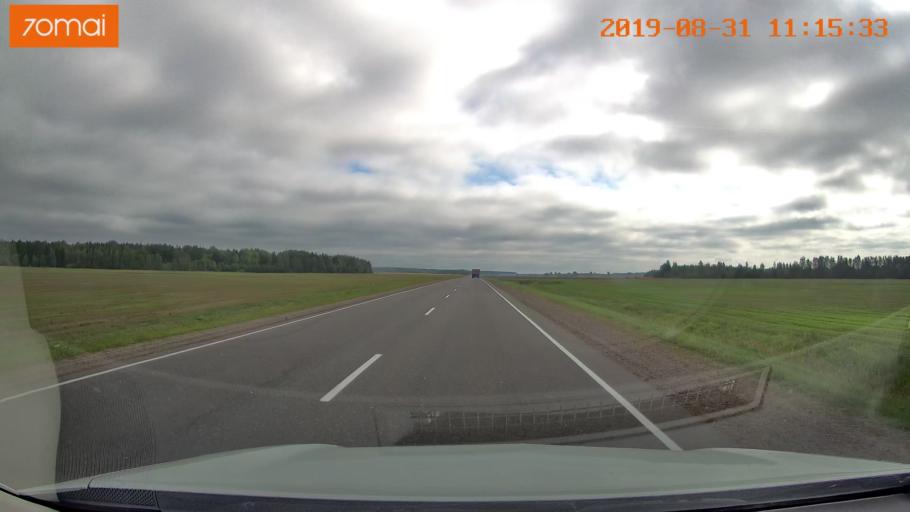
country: BY
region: Mogilev
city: Chavusy
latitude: 53.8081
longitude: 30.8586
